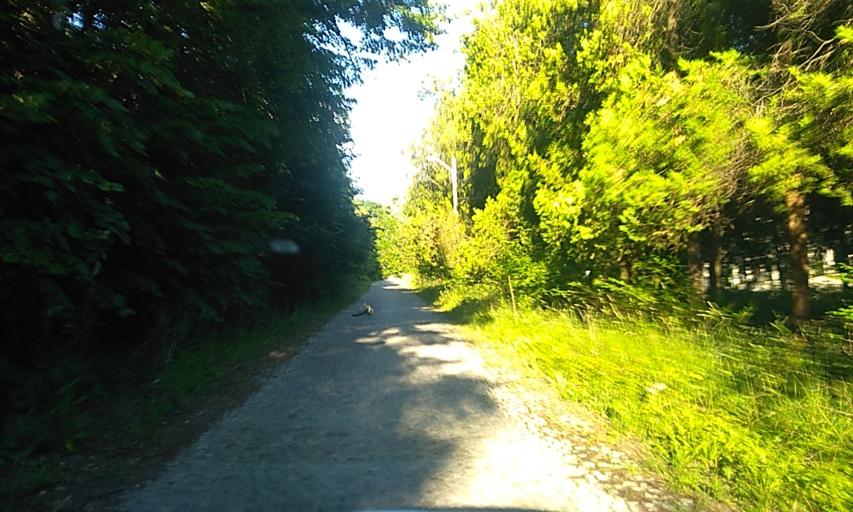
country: RS
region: Central Serbia
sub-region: Nisavski Okrug
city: Niska Banja
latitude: 43.3694
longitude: 21.9891
